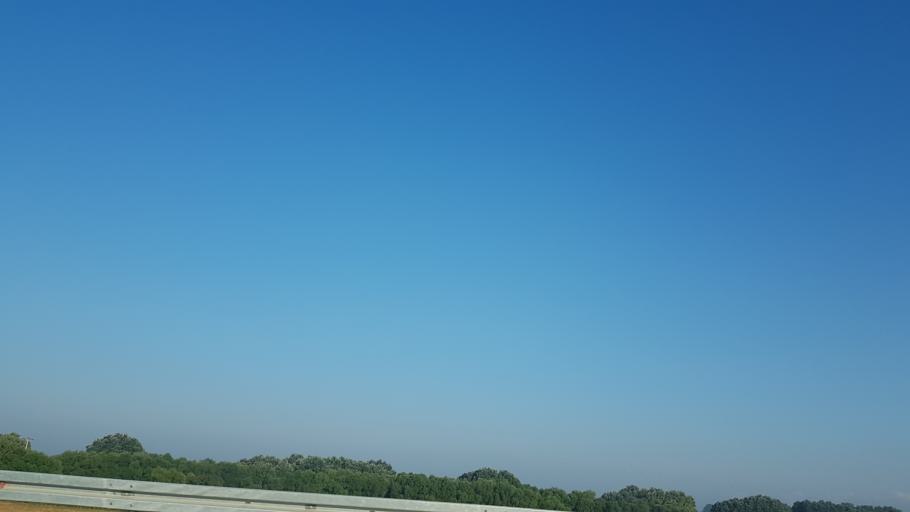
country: TR
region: Bursa
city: Karacabey
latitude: 40.1564
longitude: 28.3125
